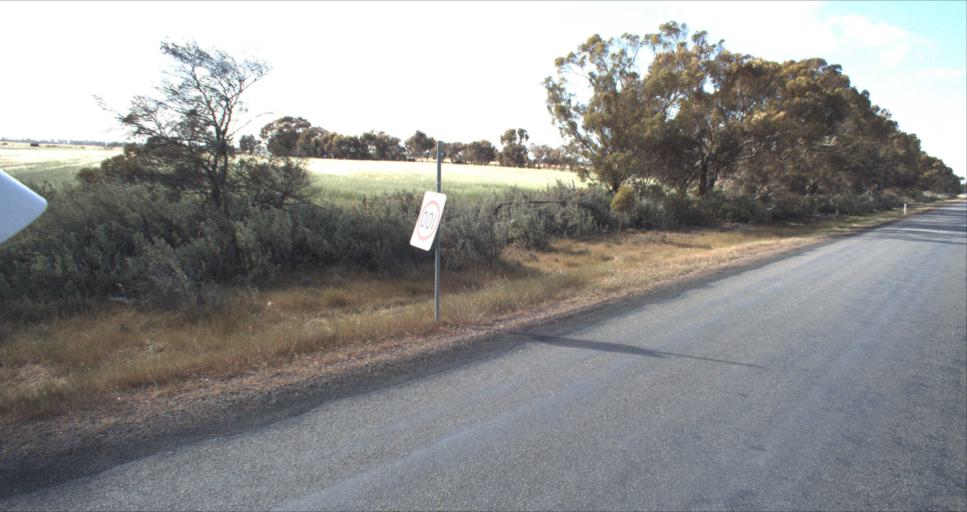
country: AU
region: New South Wales
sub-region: Leeton
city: Leeton
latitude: -34.5060
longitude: 146.3931
